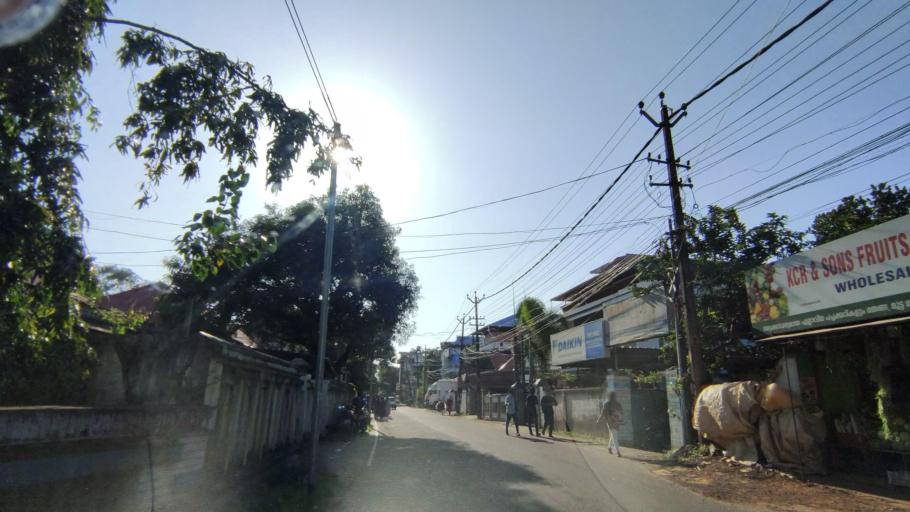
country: IN
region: Kerala
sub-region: Kottayam
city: Kottayam
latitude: 9.5904
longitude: 76.5165
